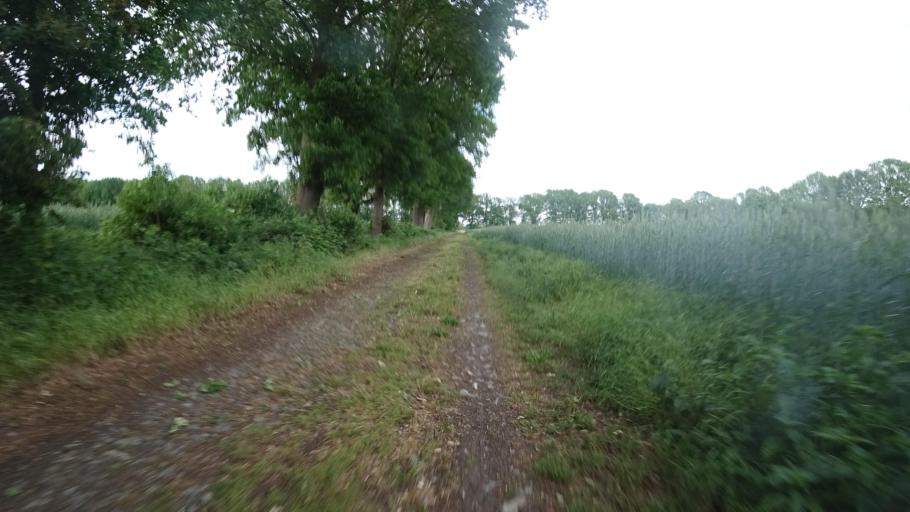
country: DE
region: North Rhine-Westphalia
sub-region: Regierungsbezirk Detmold
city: Guetersloh
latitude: 51.8723
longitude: 8.4184
